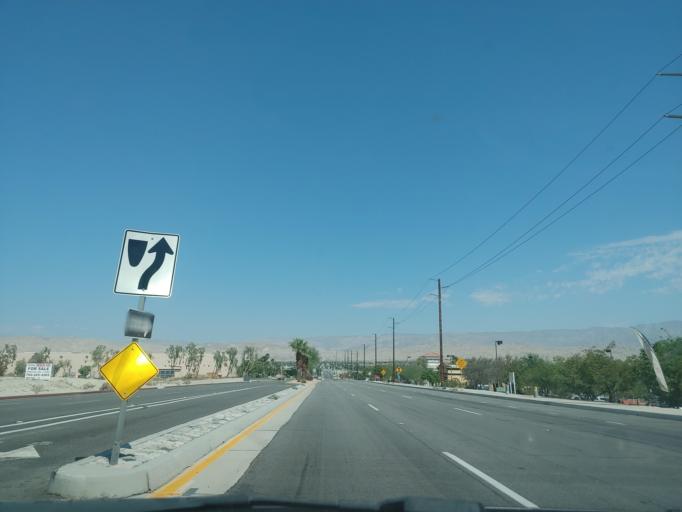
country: US
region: California
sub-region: Riverside County
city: Thousand Palms
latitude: 33.7966
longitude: -116.3881
